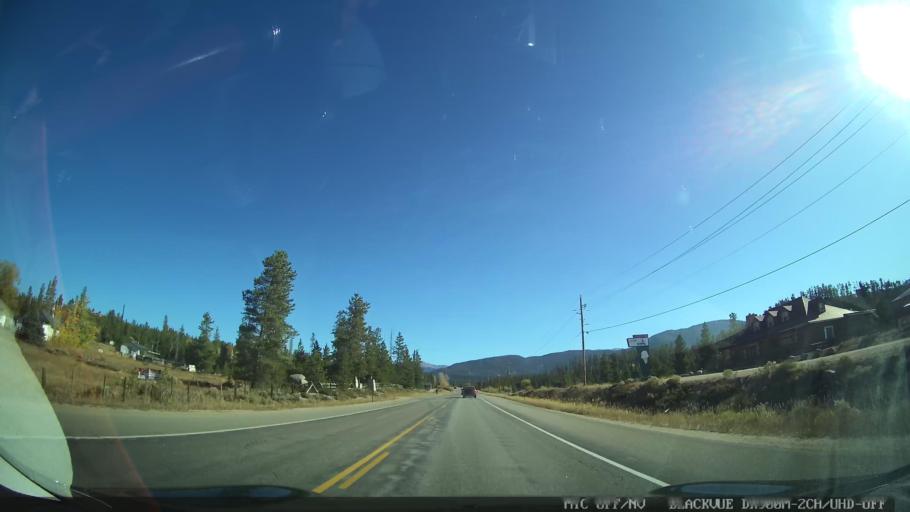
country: US
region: Colorado
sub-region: Grand County
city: Granby
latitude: 40.2003
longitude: -105.8661
